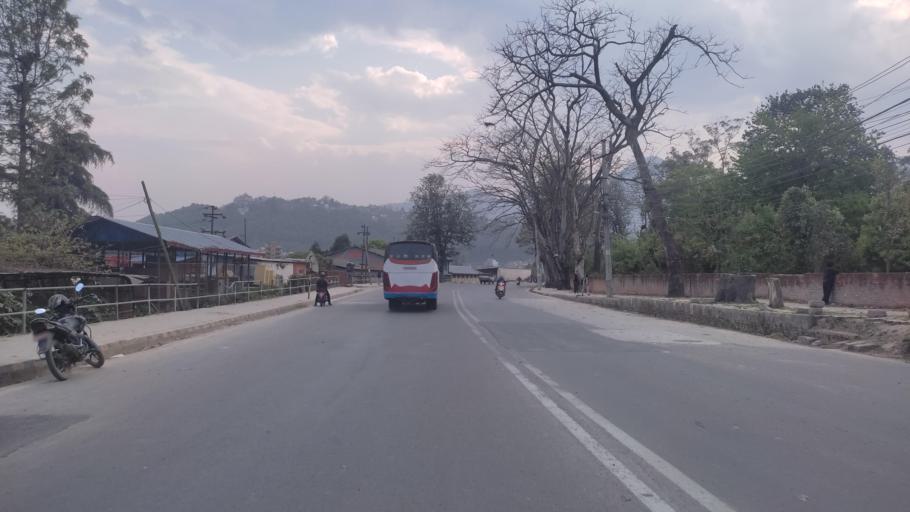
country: NP
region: Central Region
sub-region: Bagmati Zone
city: Patan
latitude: 27.6785
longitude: 85.2970
